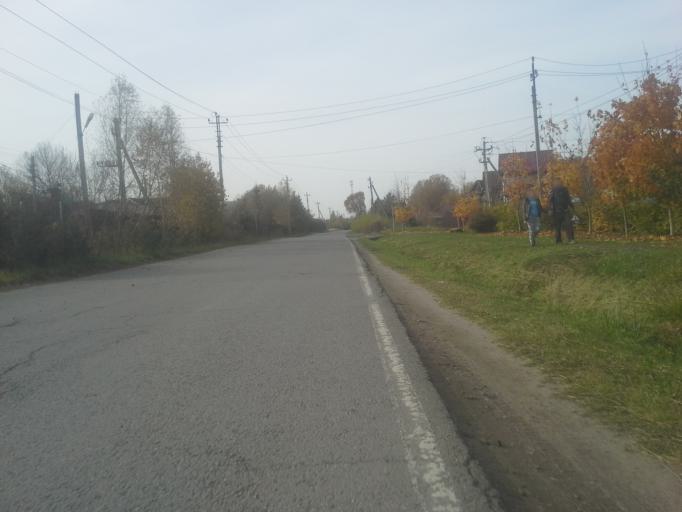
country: RU
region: Moskovskaya
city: Aprelevka
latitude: 55.5581
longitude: 37.0530
